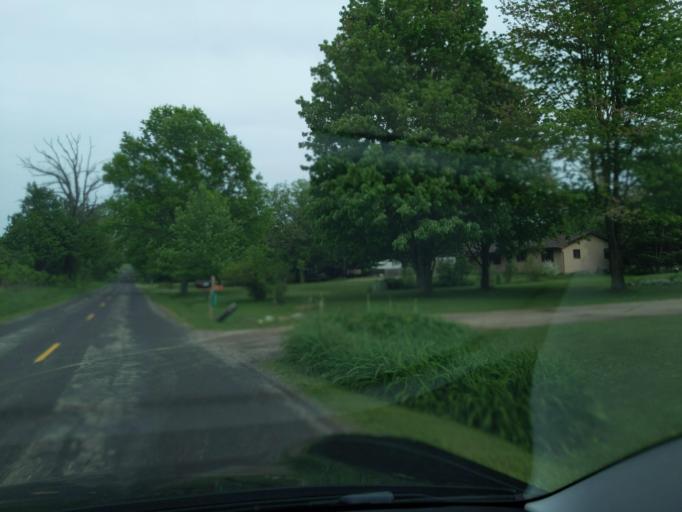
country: US
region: Michigan
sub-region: Ingham County
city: Leslie
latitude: 42.4657
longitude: -84.4401
